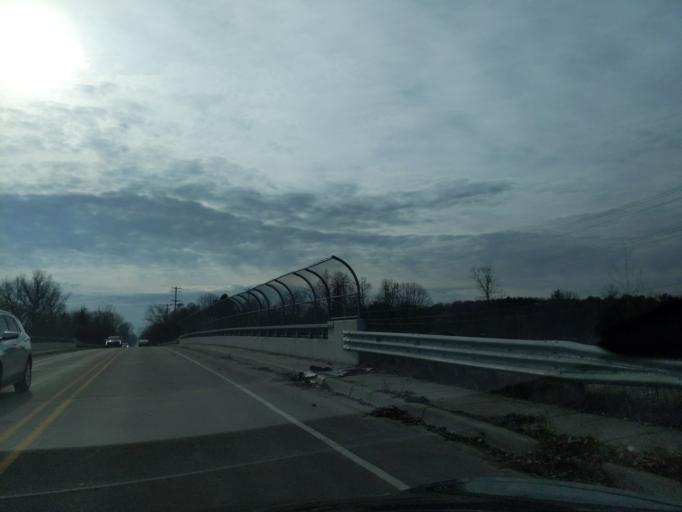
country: US
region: Michigan
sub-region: Ingham County
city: Holt
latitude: 42.6648
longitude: -84.5236
